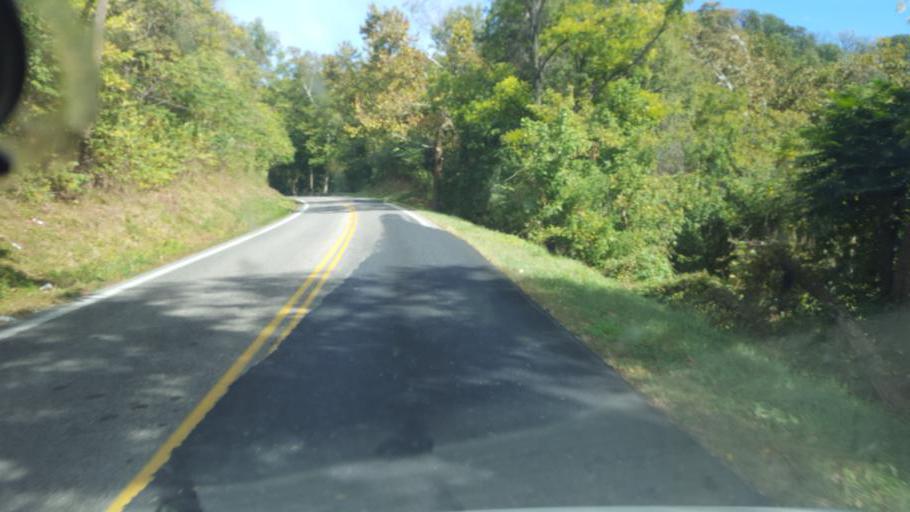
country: US
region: Virginia
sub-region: Page County
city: Stanley
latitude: 38.5838
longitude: -78.5939
